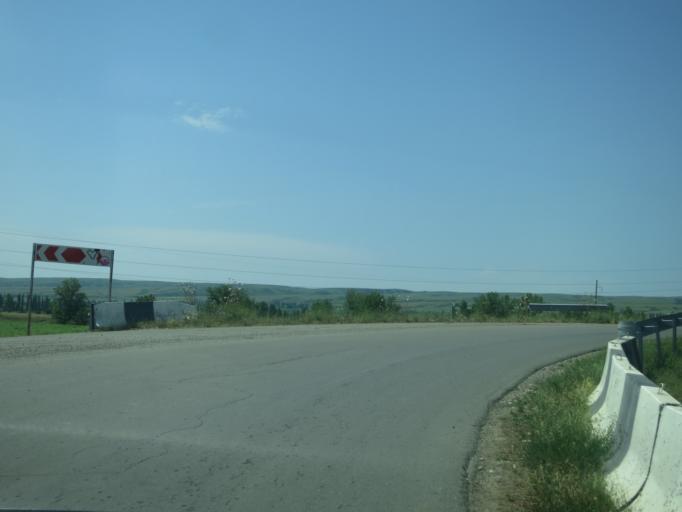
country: GE
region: Kakheti
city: Sagarejo
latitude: 41.6680
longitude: 45.3901
